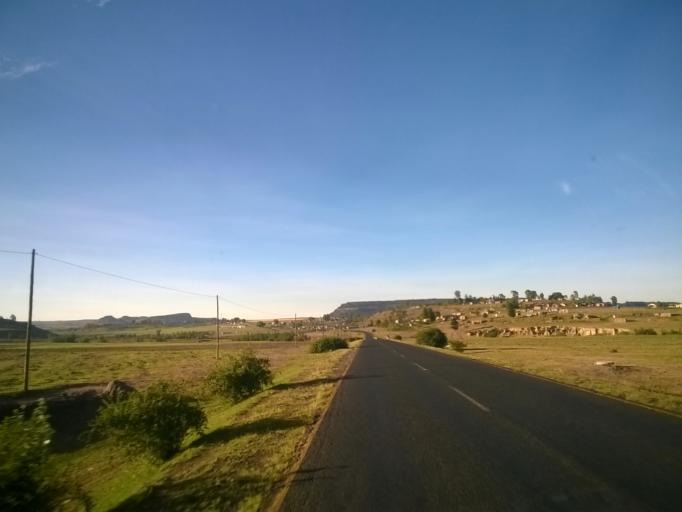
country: LS
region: Berea
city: Teyateyaneng
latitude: -29.1914
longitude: 27.6223
